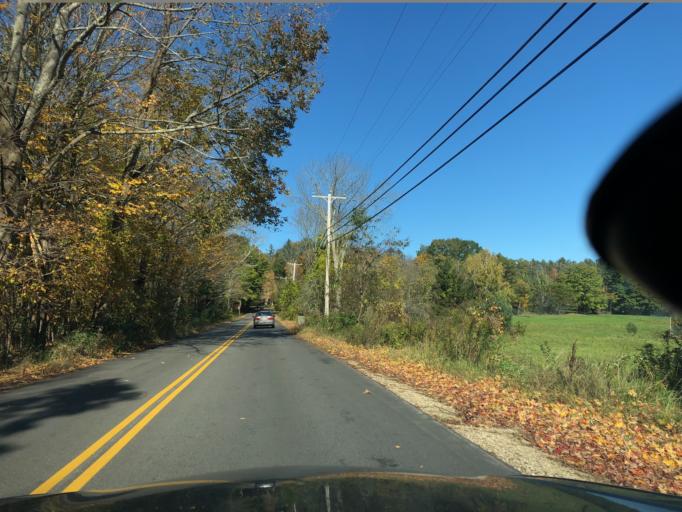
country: US
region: New Hampshire
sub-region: Rockingham County
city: Newmarket
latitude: 43.1097
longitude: -70.9589
